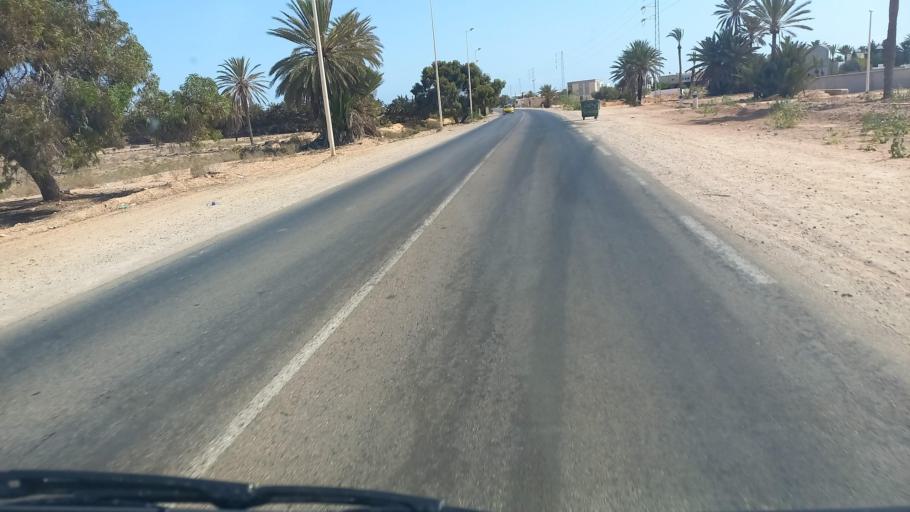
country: TN
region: Madanin
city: Midoun
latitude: 33.7708
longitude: 11.0246
